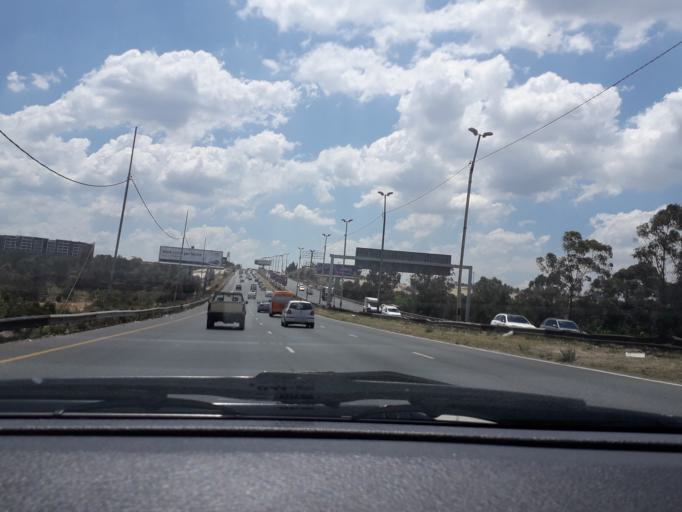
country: ZA
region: Gauteng
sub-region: City of Johannesburg Metropolitan Municipality
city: Johannesburg
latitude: -26.2290
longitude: 28.0193
